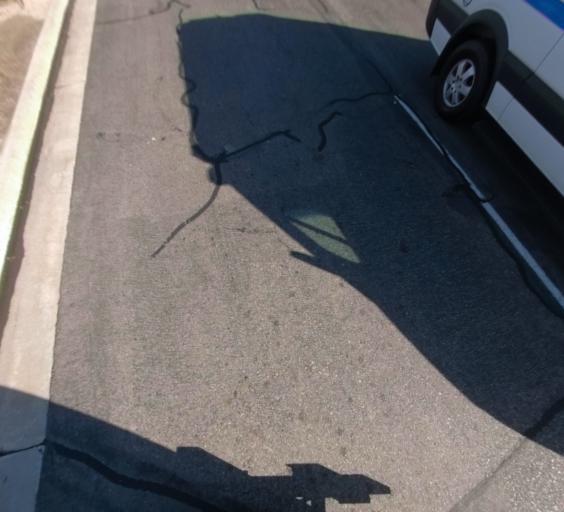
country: US
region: California
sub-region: Fresno County
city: Clovis
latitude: 36.8847
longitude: -119.8008
